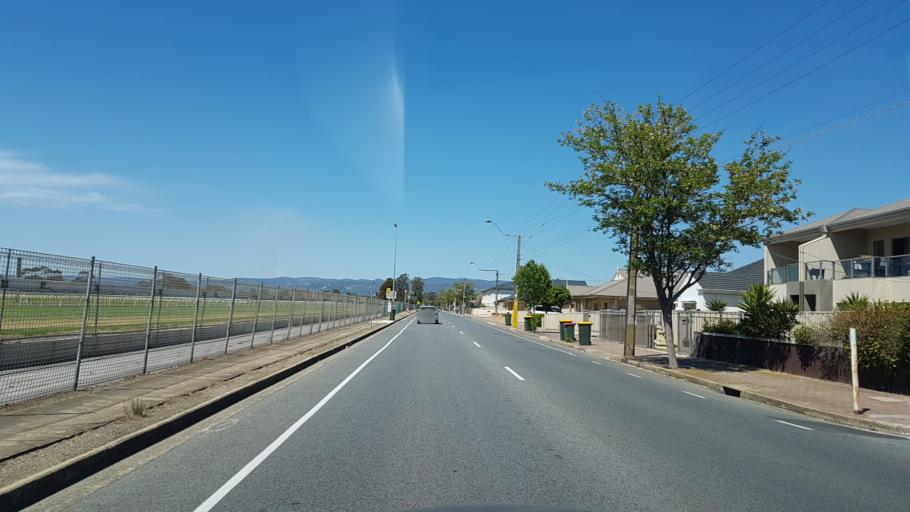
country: AU
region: South Australia
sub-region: Marion
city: Plympton Park
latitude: -34.9812
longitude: 138.5417
